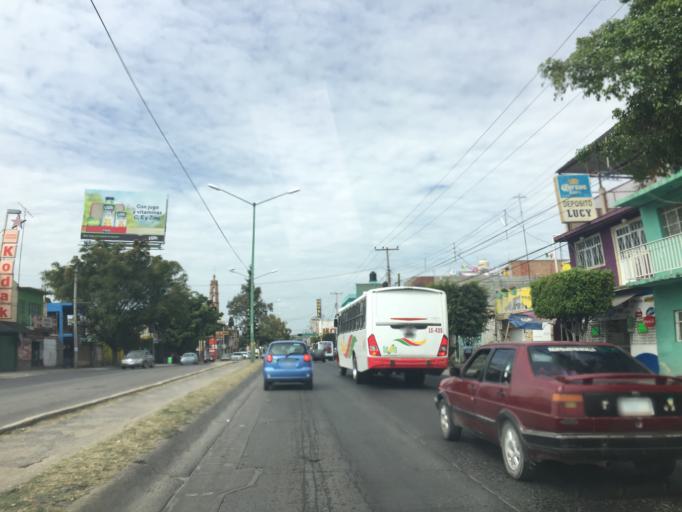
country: MX
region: Guanajuato
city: Leon
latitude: 21.1014
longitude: -101.6818
